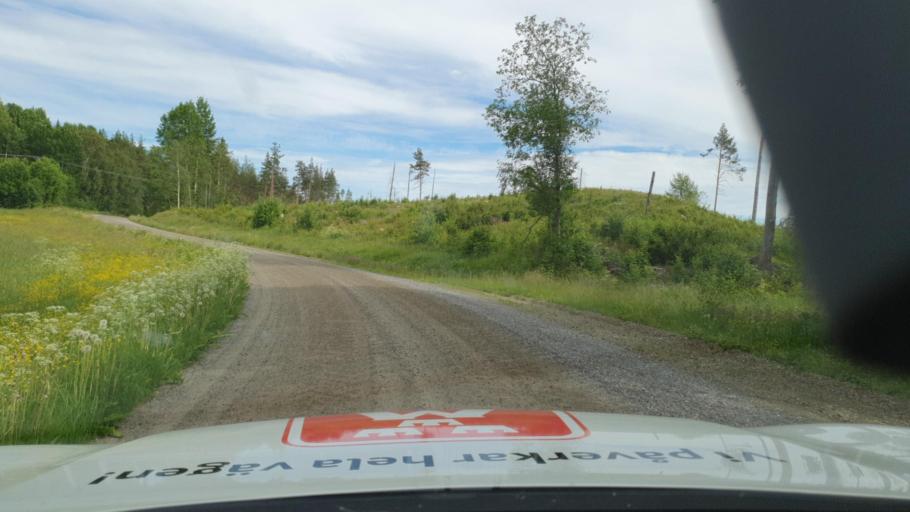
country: SE
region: Vaesterbotten
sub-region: Robertsfors Kommun
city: Robertsfors
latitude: 64.3915
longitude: 21.0235
